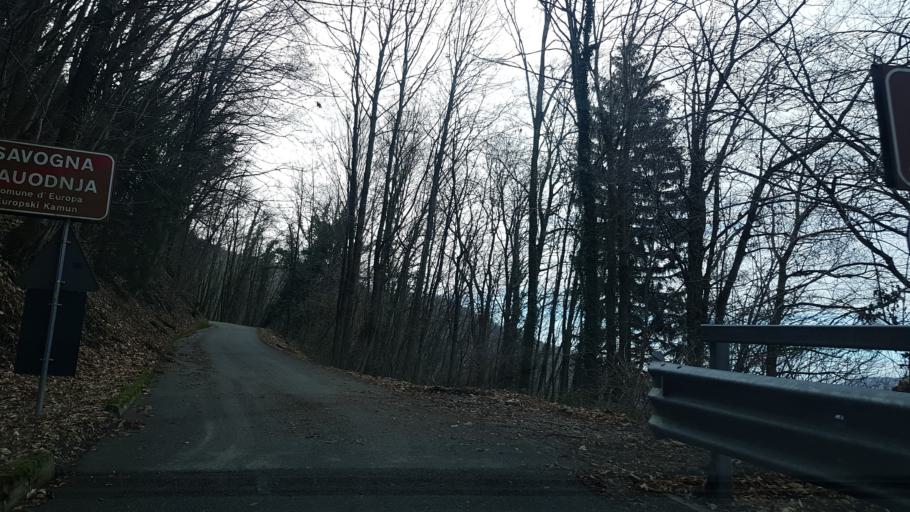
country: IT
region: Friuli Venezia Giulia
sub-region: Provincia di Udine
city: Clodig
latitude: 46.1750
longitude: 13.5766
